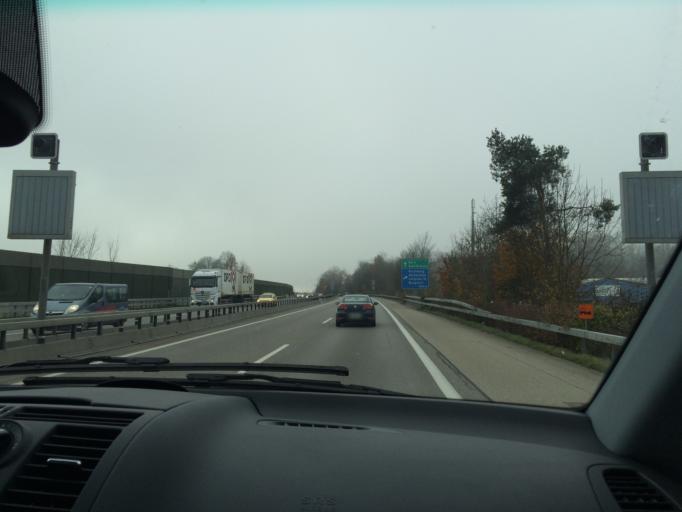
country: CH
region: Bern
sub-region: Emmental District
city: Kirchberg
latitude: 47.0940
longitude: 7.5733
